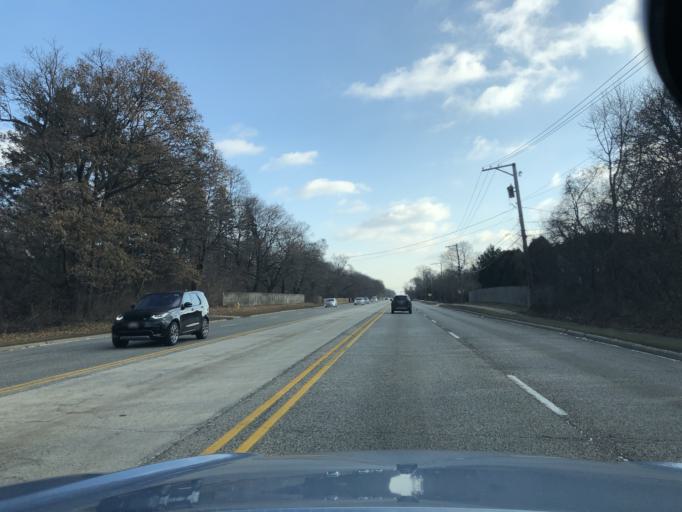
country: US
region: Illinois
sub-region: Cook County
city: Northbrook
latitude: 42.1058
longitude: -87.8559
